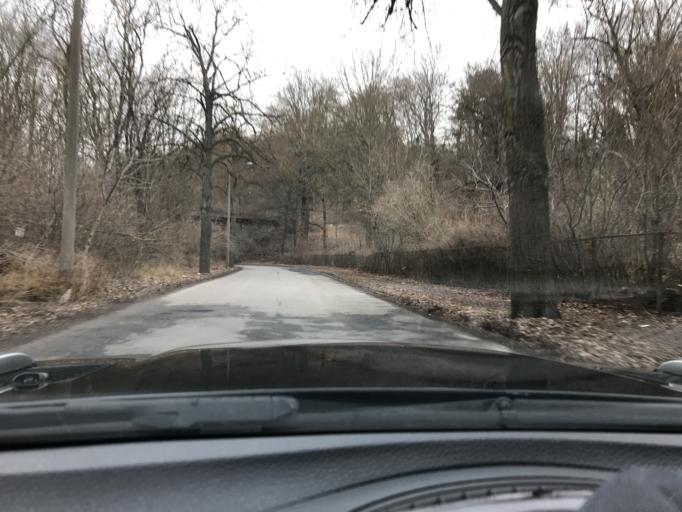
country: DE
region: Thuringia
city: Muehlhausen
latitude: 51.2050
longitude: 10.4819
